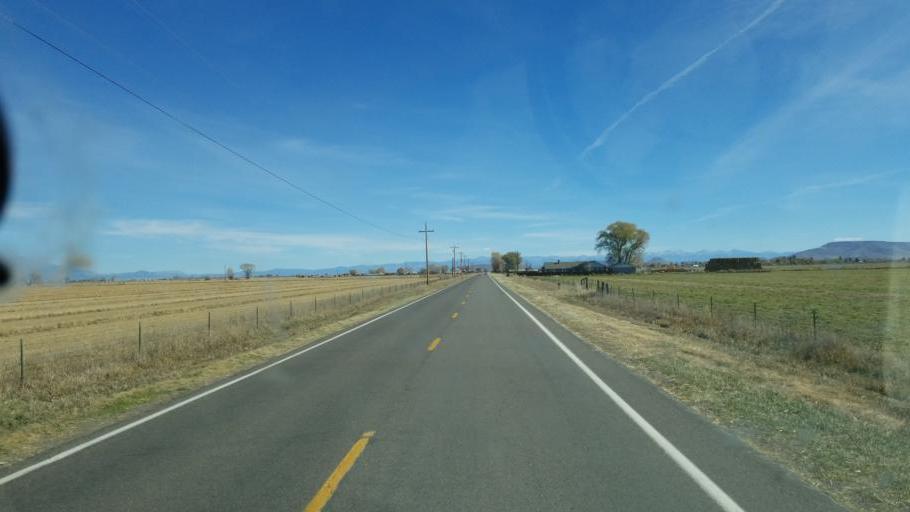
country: US
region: Colorado
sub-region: Conejos County
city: Conejos
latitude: 37.2835
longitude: -105.9911
